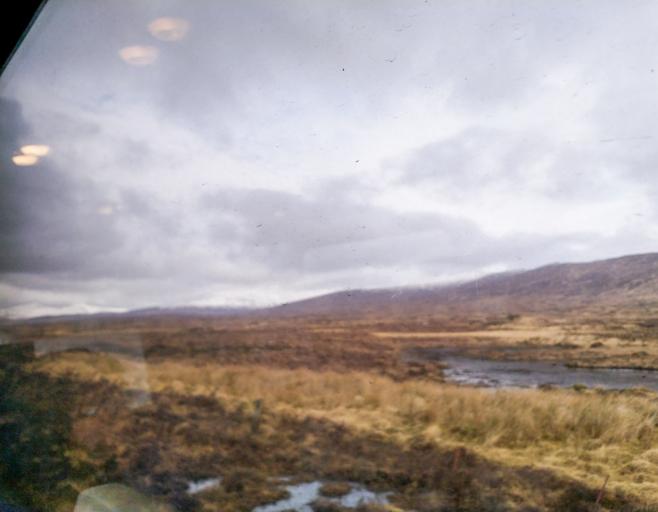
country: GB
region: Scotland
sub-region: Highland
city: Spean Bridge
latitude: 56.7050
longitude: -4.5906
